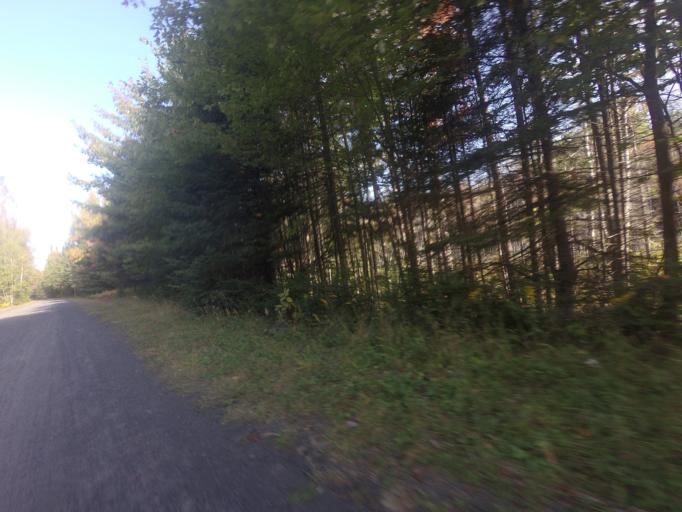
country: CA
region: Quebec
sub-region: Laurentides
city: Val-David
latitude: 46.0122
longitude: -74.1758
